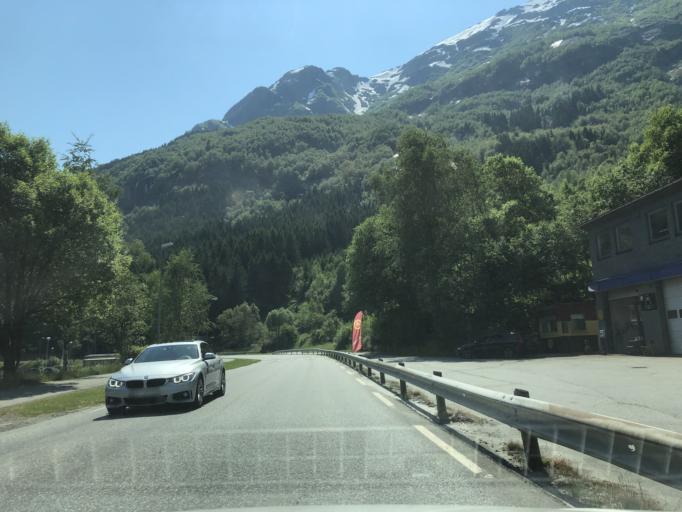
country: NO
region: Hordaland
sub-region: Odda
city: Odda
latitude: 60.0806
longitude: 6.5301
